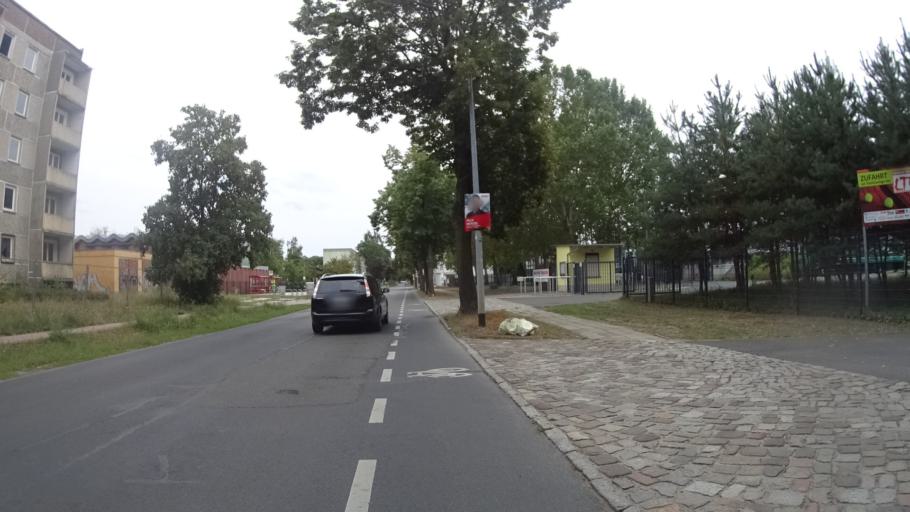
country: DE
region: Brandenburg
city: Luckenwalde
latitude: 52.1042
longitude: 13.1492
